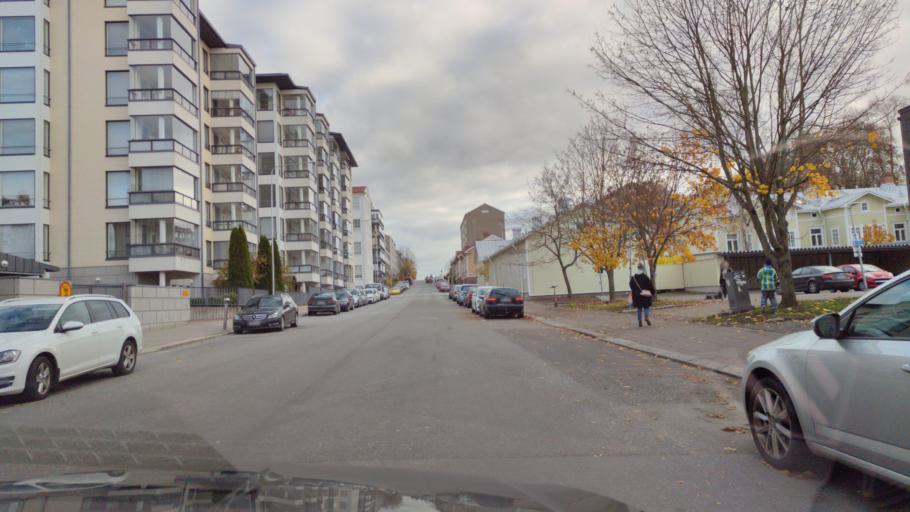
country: FI
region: Varsinais-Suomi
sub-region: Turku
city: Turku
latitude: 60.4405
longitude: 22.2493
